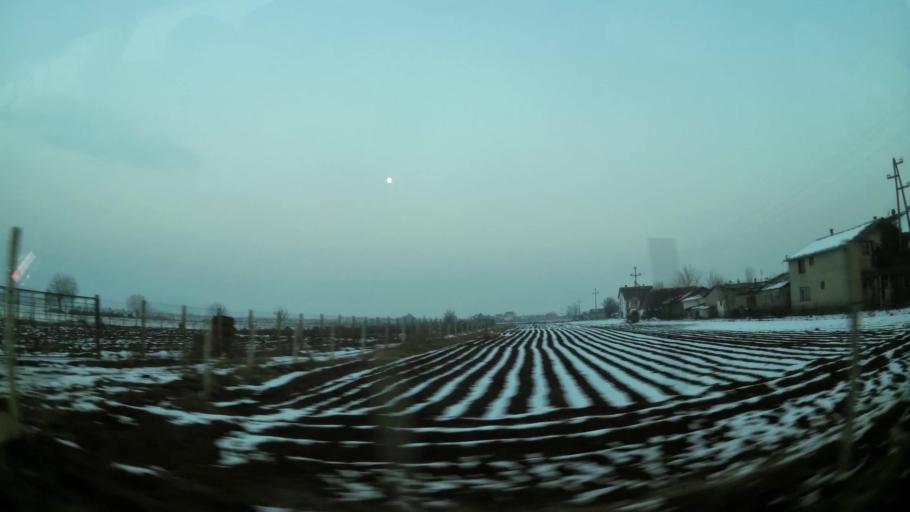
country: MK
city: Creshevo
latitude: 42.0075
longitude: 21.5175
